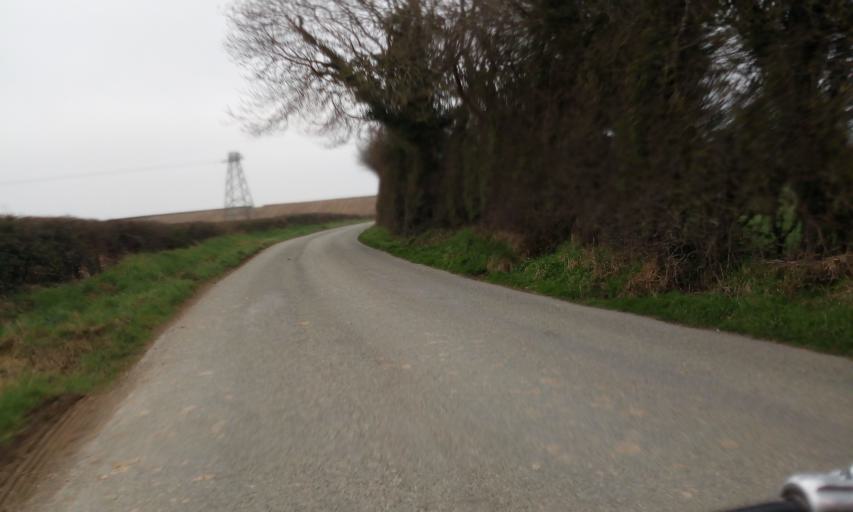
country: IE
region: Leinster
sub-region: Kilkenny
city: Kilkenny
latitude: 52.6581
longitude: -7.1735
